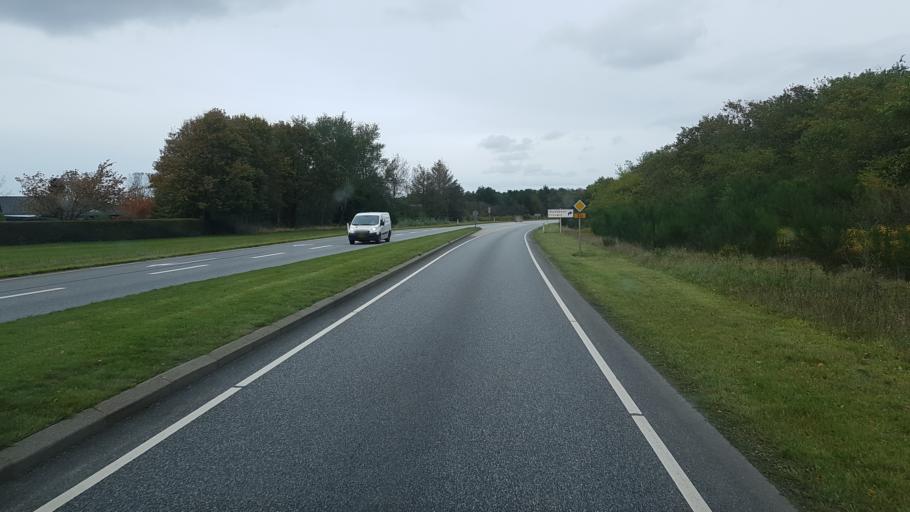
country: DK
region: South Denmark
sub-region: Billund Kommune
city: Grindsted
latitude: 55.7470
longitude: 8.9247
